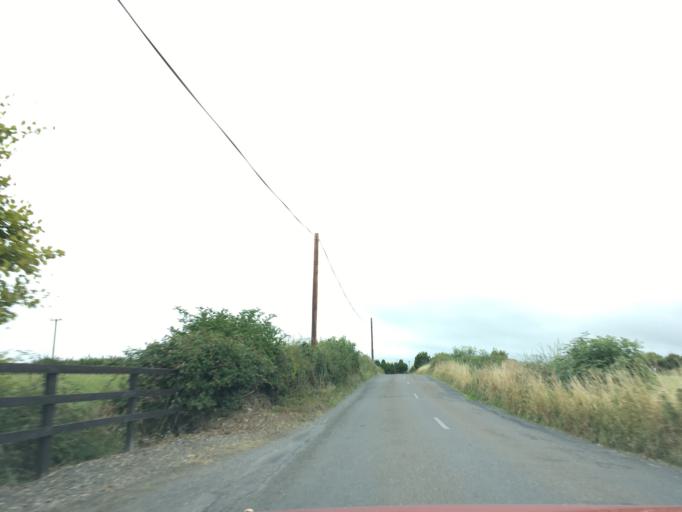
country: IE
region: Munster
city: Cashel
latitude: 52.4764
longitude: -7.8898
